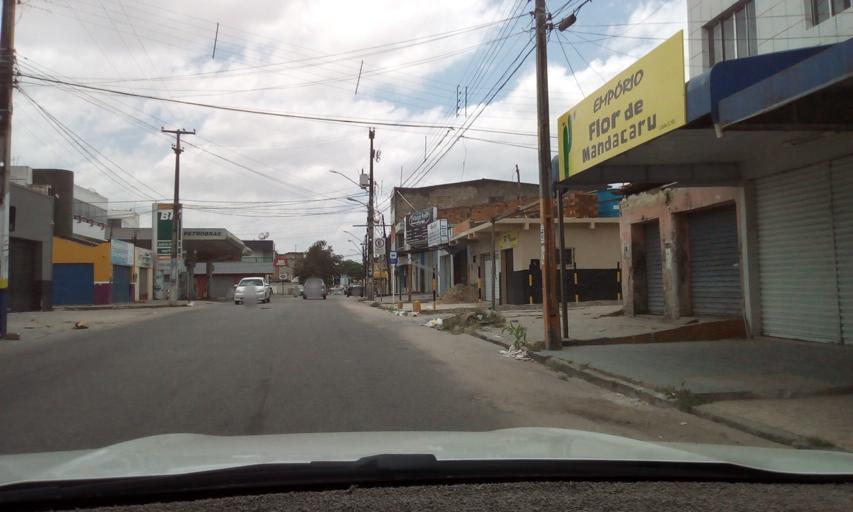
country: BR
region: Pernambuco
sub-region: Caruaru
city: Caruaru
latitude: -8.2715
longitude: -35.9842
